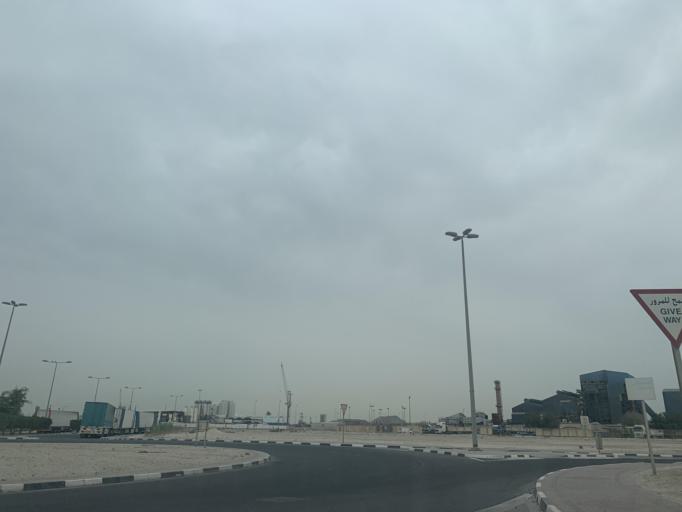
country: BH
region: Muharraq
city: Al Hadd
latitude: 26.2107
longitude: 50.6728
